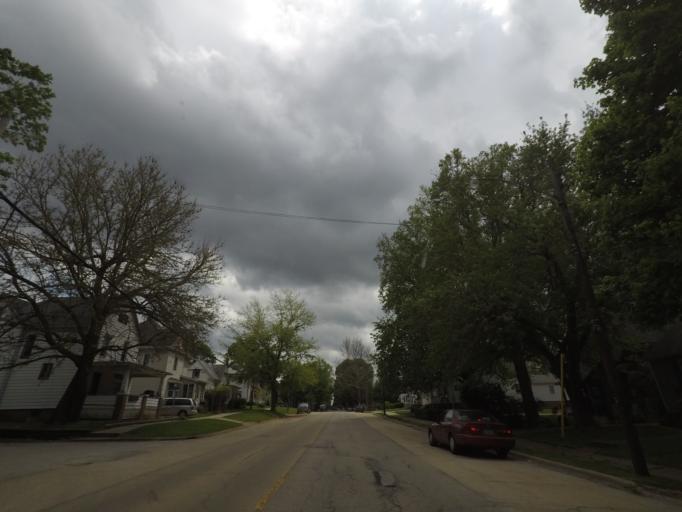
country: US
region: Illinois
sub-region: De Witt County
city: Clinton
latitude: 40.1592
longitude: -88.9606
